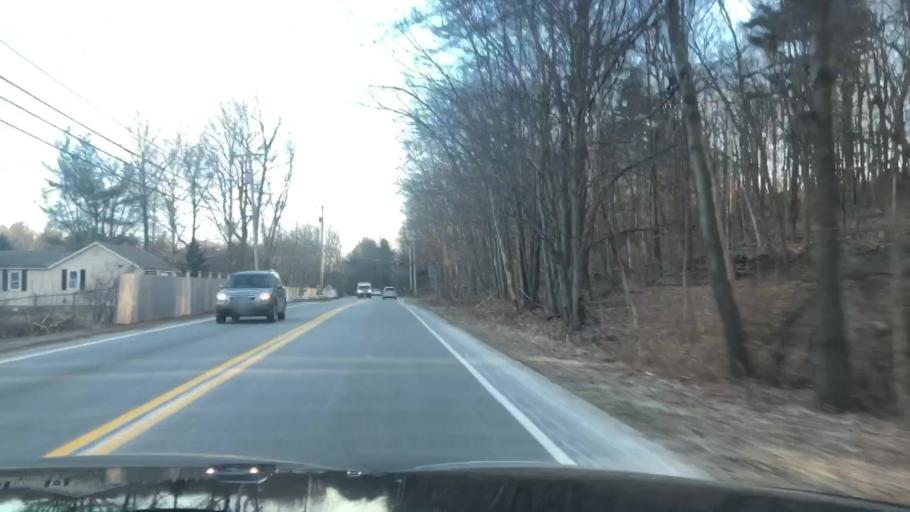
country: US
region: Massachusetts
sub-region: Worcester County
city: Bolton
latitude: 42.4416
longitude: -71.6208
